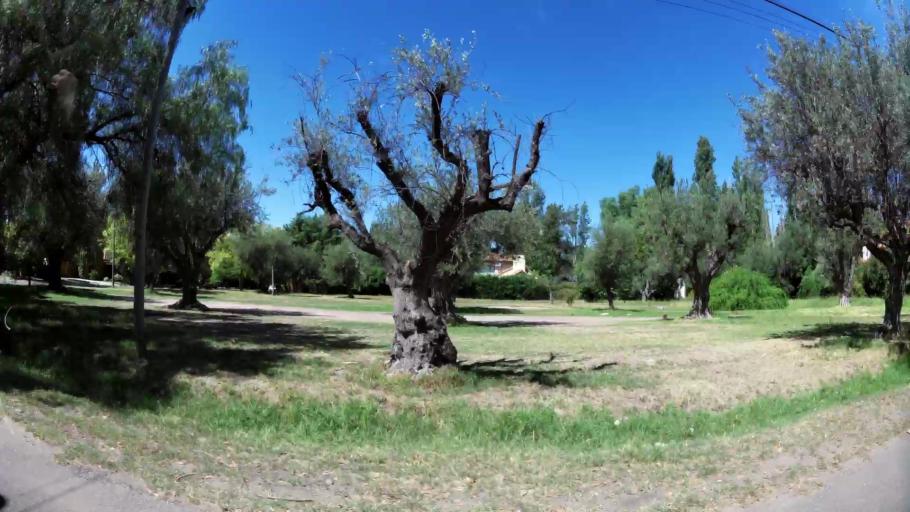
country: AR
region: Mendoza
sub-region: Departamento de Godoy Cruz
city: Godoy Cruz
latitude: -32.9693
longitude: -68.8718
